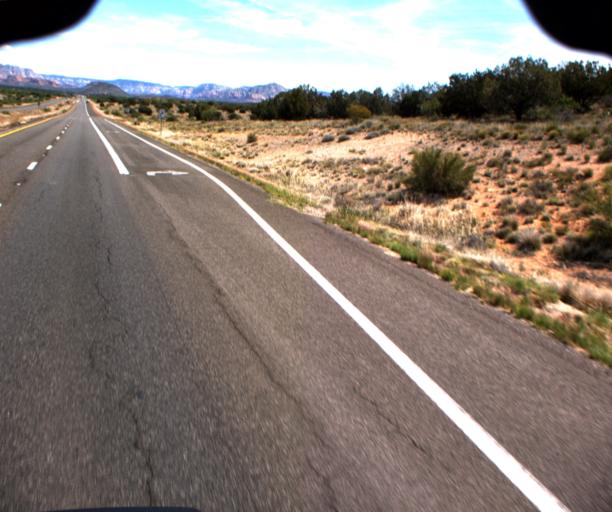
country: US
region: Arizona
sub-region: Yavapai County
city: Cornville
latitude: 34.8078
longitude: -111.9092
